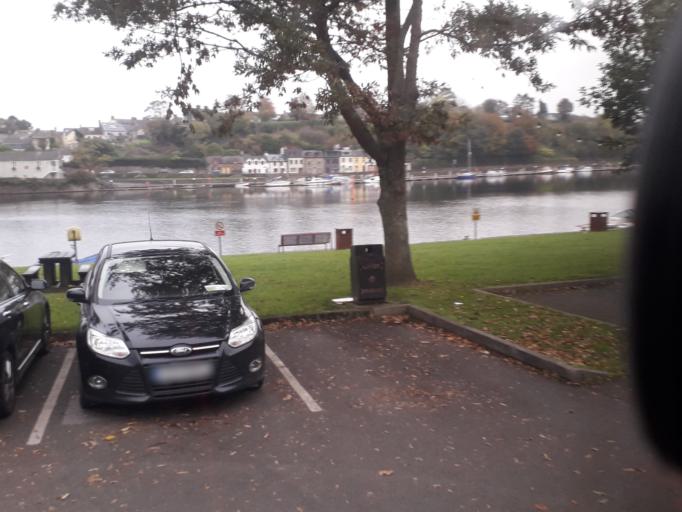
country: IE
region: Munster
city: Ballina
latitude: 52.8094
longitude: -8.4390
